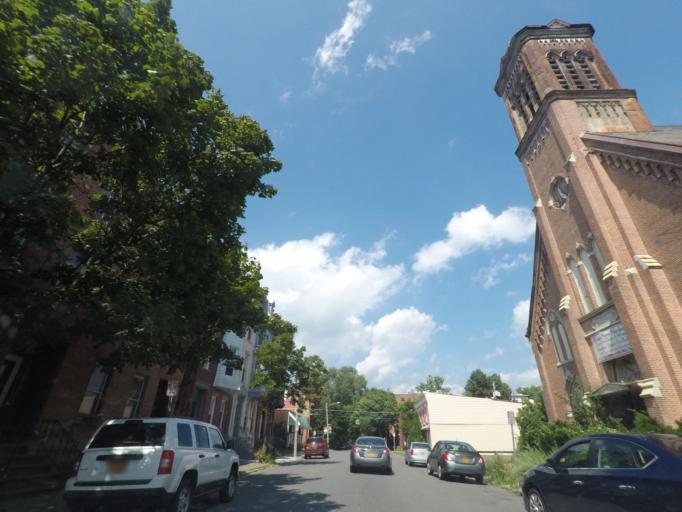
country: US
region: New York
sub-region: Rensselaer County
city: Troy
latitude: 42.7224
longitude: -73.6935
